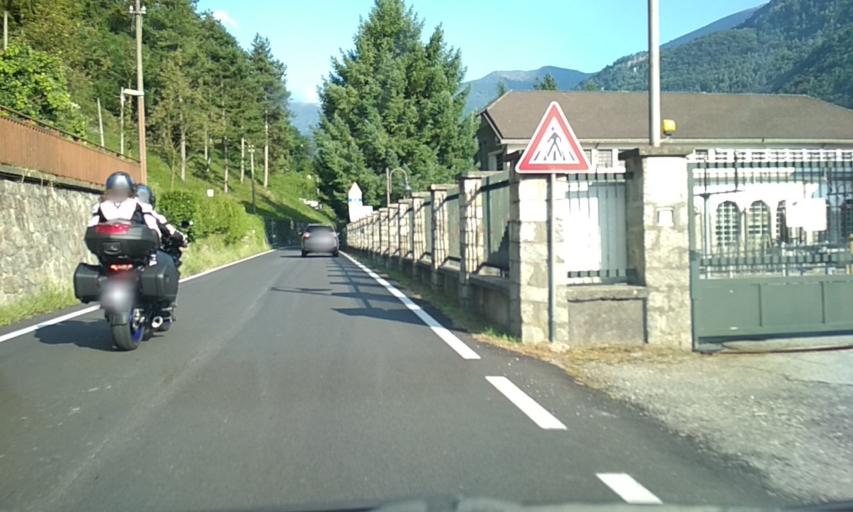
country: IT
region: Piedmont
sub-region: Provincia di Torino
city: Ribordone
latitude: 45.4093
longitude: 7.4865
